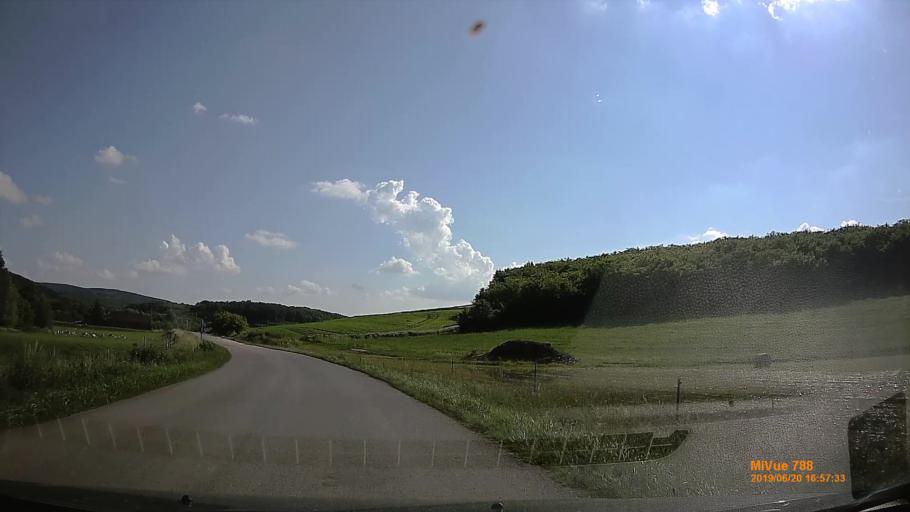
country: HU
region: Baranya
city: Buekkoesd
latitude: 46.1430
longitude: 18.0601
